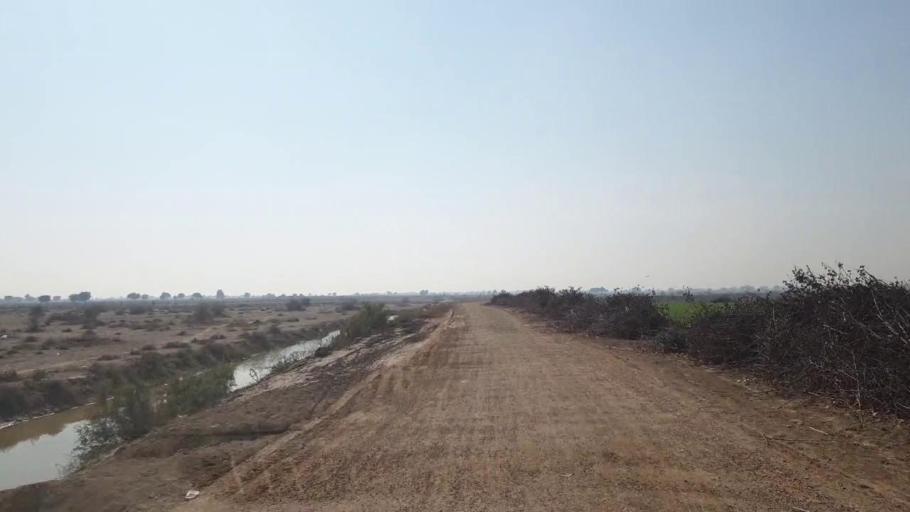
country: PK
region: Sindh
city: Shahpur Chakar
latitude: 26.1162
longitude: 68.6110
